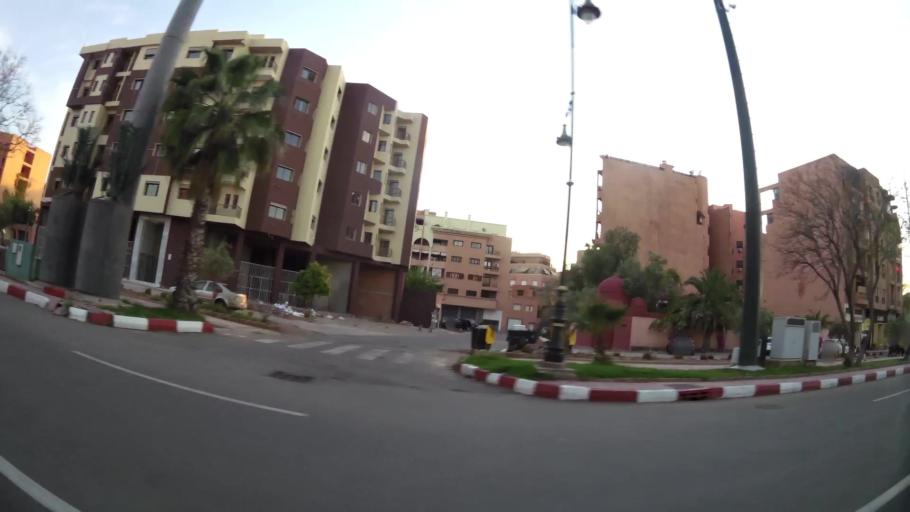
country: MA
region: Marrakech-Tensift-Al Haouz
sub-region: Marrakech
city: Marrakesh
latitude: 31.6394
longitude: -8.0221
